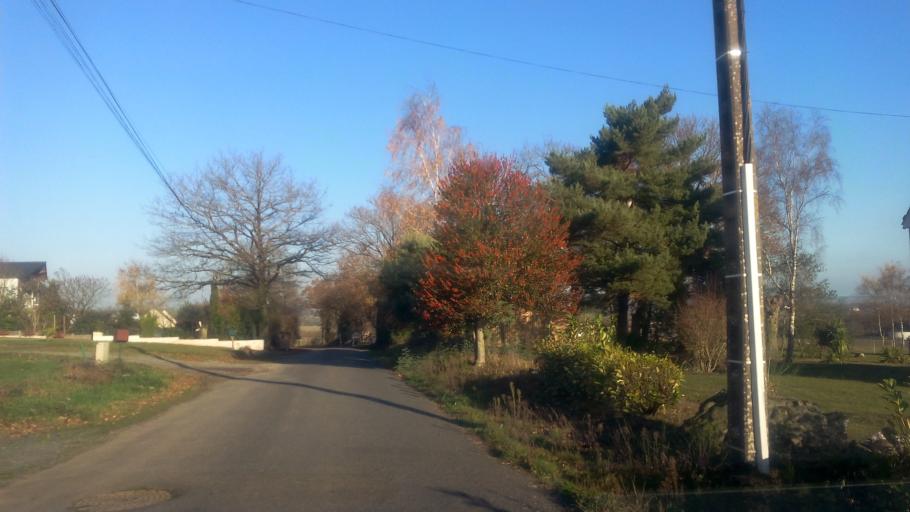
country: FR
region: Pays de la Loire
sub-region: Departement de la Loire-Atlantique
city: Avessac
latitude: 47.6573
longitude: -1.9936
